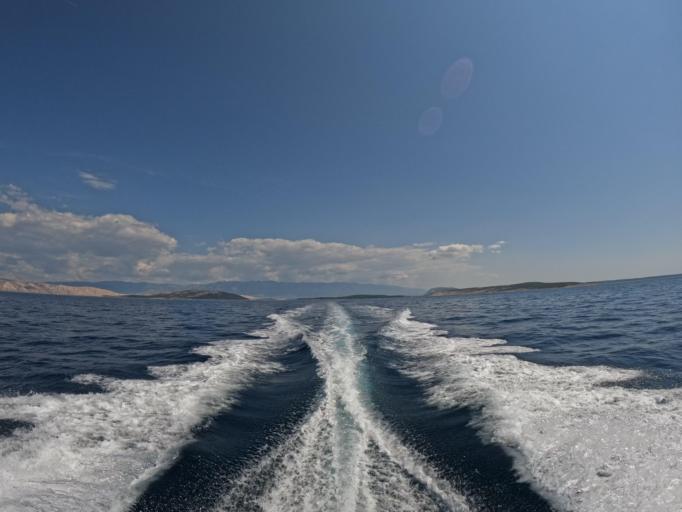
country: HR
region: Primorsko-Goranska
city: Lopar
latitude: 44.8718
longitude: 14.6706
